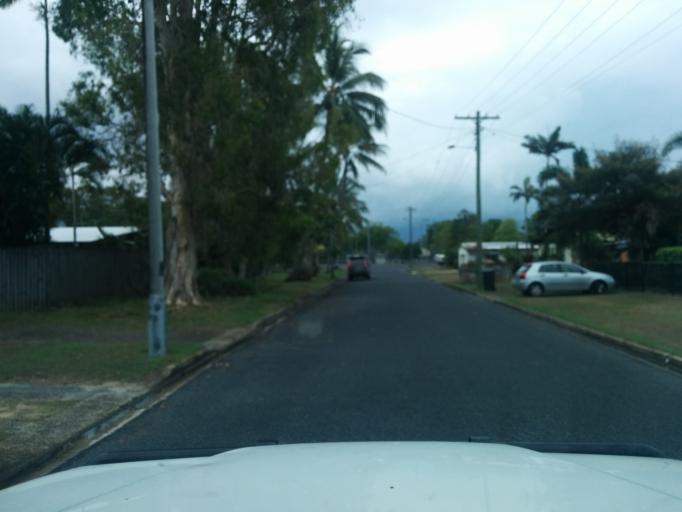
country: AU
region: Queensland
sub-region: Cairns
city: Yorkeys Knob
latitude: -16.8434
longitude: 145.7404
